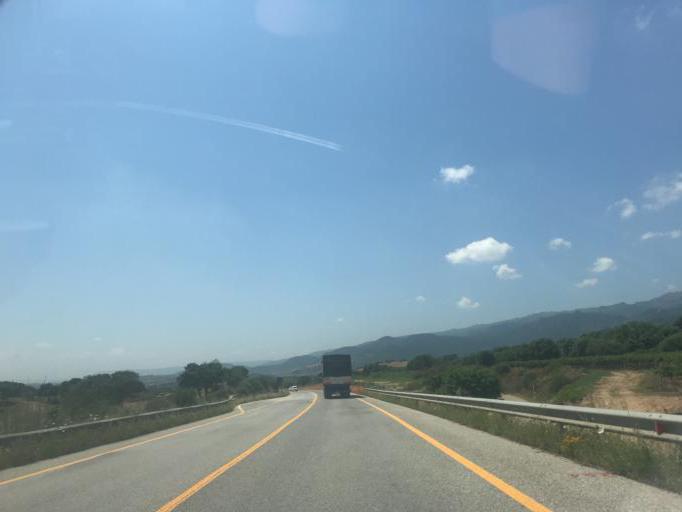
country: IT
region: Sardinia
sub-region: Provincia di Olbia-Tempio
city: Berchidda
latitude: 40.7812
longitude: 9.2210
